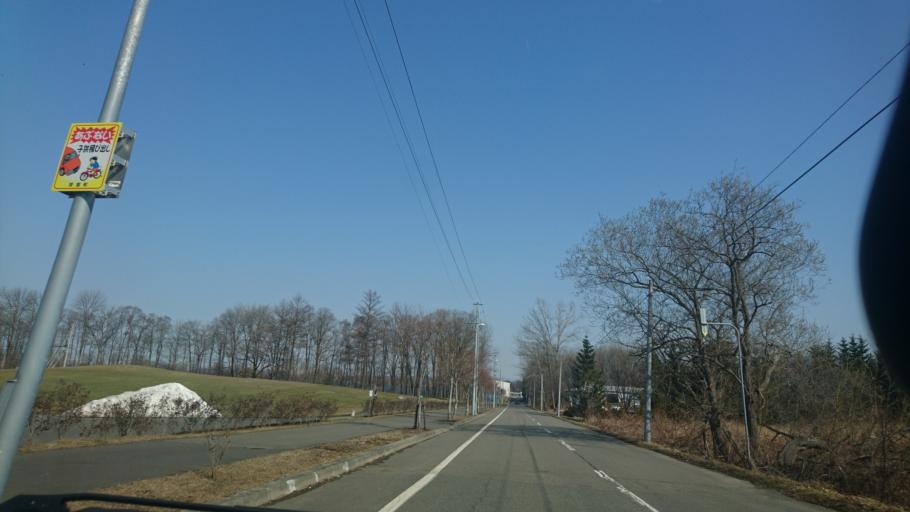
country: JP
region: Hokkaido
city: Obihiro
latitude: 42.9159
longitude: 143.0764
